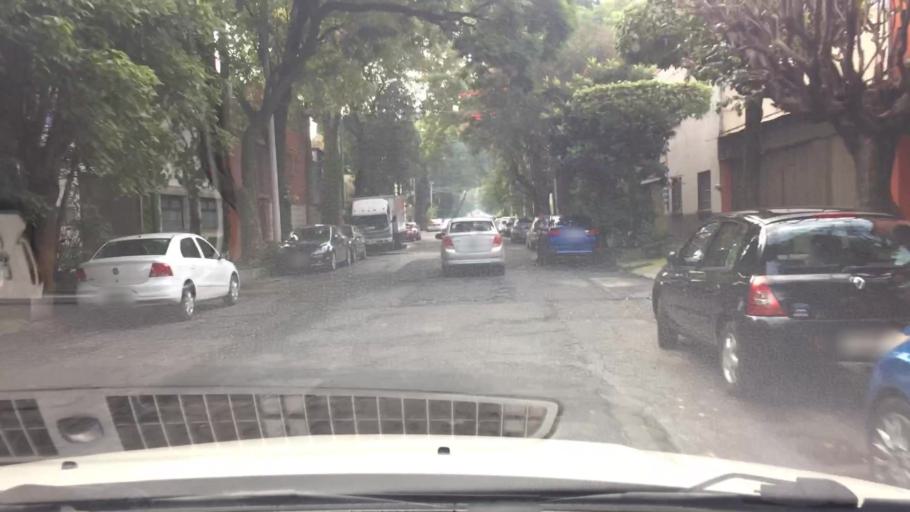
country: MX
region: Mexico City
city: Coyoacan
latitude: 19.3566
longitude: -99.1579
